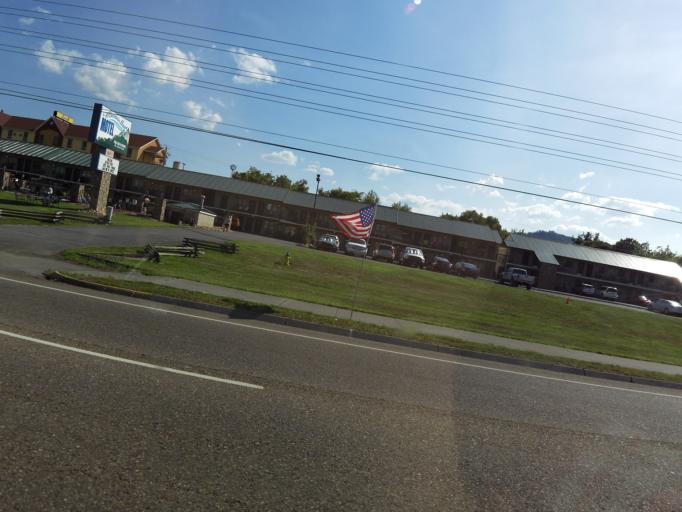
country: US
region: Tennessee
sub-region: Sevier County
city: Pigeon Forge
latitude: 35.7965
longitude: -83.5655
